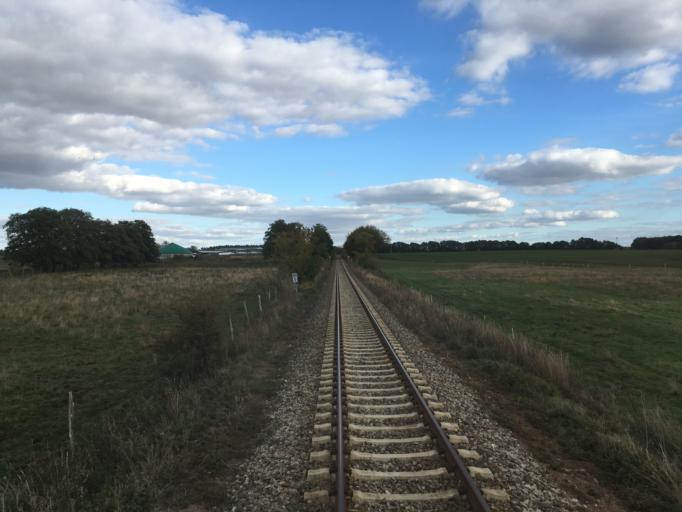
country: DE
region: Mecklenburg-Vorpommern
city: Grabowhofe
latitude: 53.5408
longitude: 12.5942
